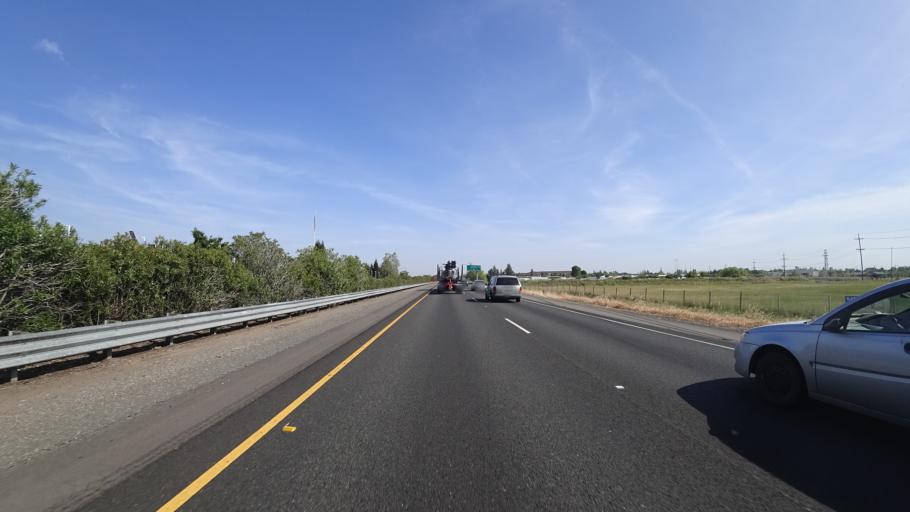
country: US
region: California
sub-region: Butte County
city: Chico
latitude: 39.7206
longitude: -121.8052
